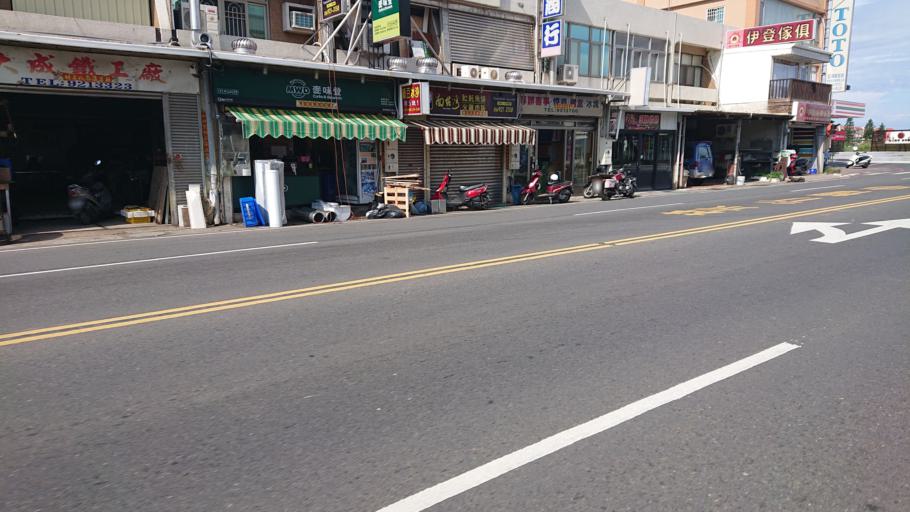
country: TW
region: Taiwan
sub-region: Penghu
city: Ma-kung
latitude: 23.5596
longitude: 119.5977
